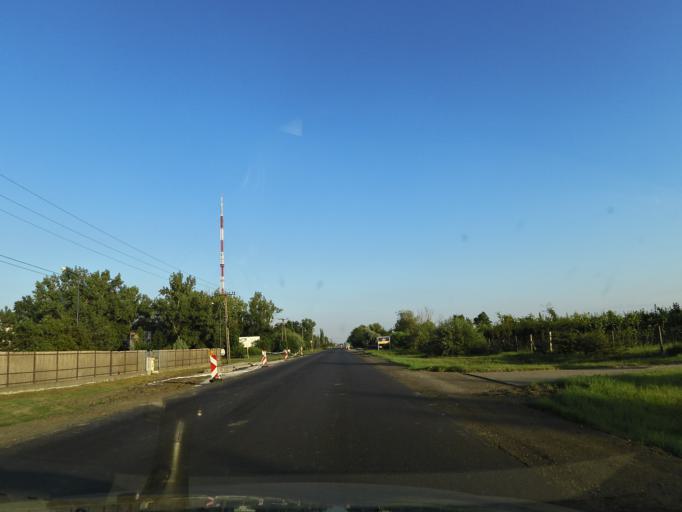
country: HU
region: Csongrad
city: Szentes
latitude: 46.6288
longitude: 20.2764
